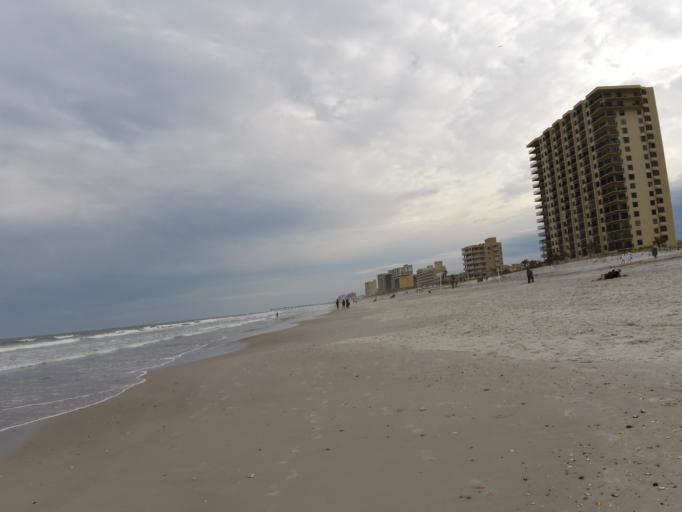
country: US
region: Florida
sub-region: Duval County
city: Neptune Beach
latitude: 30.3083
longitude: -81.3918
